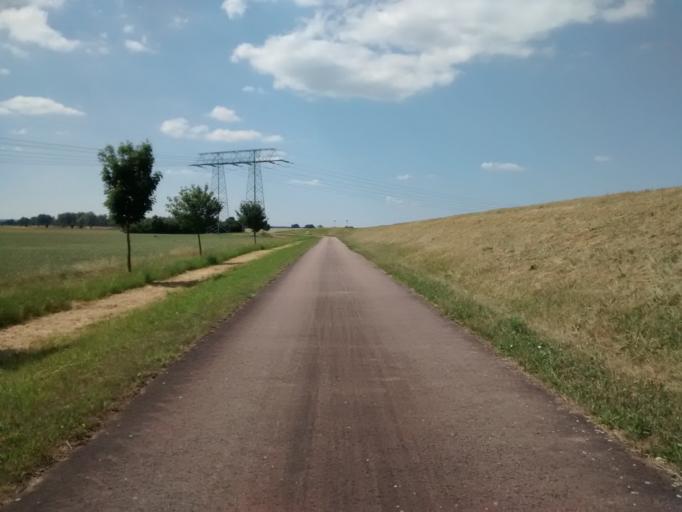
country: DE
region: Saxony-Anhalt
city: Coswig
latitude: 51.8410
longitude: 12.5199
